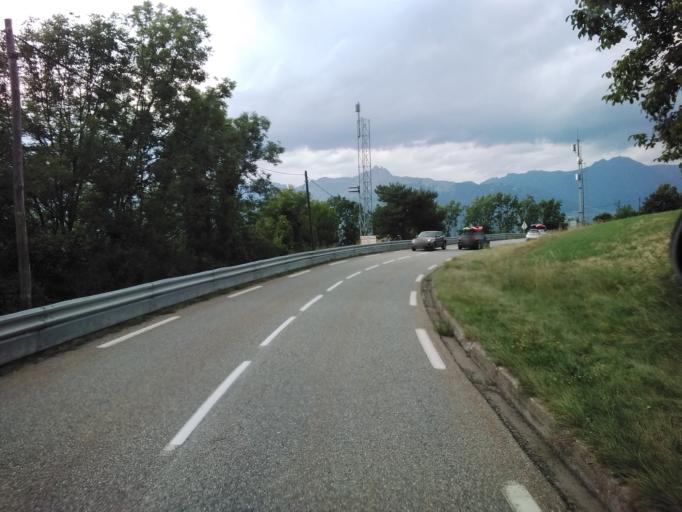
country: FR
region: Provence-Alpes-Cote d'Azur
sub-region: Departement des Hautes-Alpes
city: Chorges
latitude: 44.4982
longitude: 6.3436
